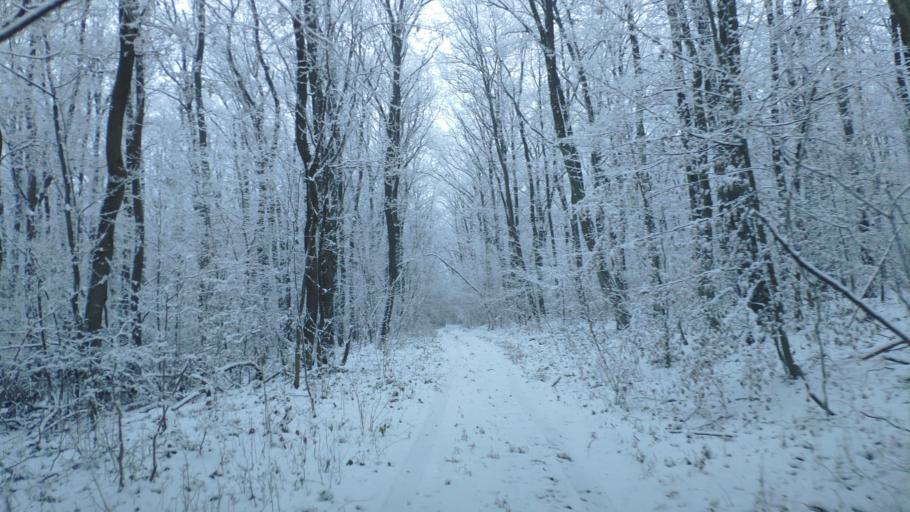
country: SK
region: Kosicky
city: Kosice
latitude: 48.6465
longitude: 21.1802
